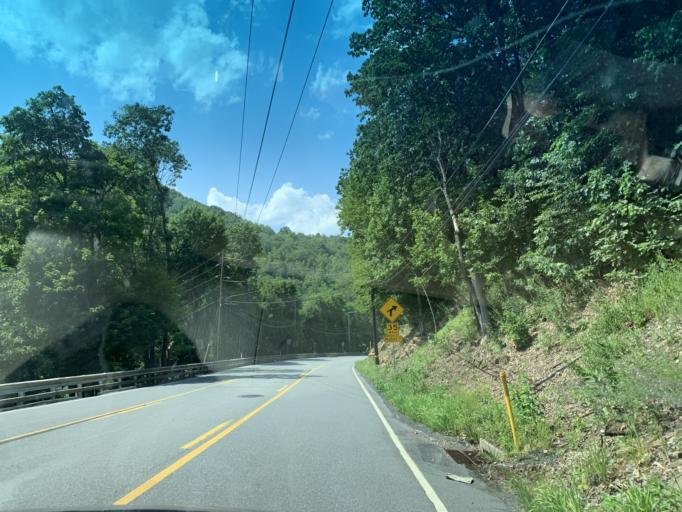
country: US
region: Pennsylvania
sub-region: Schuylkill County
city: Ashland
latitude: 40.7738
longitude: -76.3384
